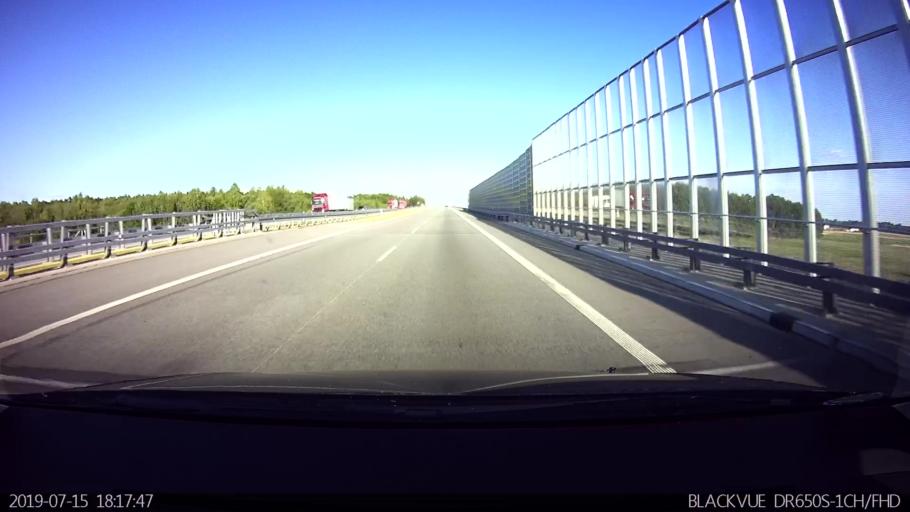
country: PL
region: Lodz Voivodeship
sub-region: Powiat zdunskowolski
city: Zdunska Wola
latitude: 51.5682
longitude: 18.9746
